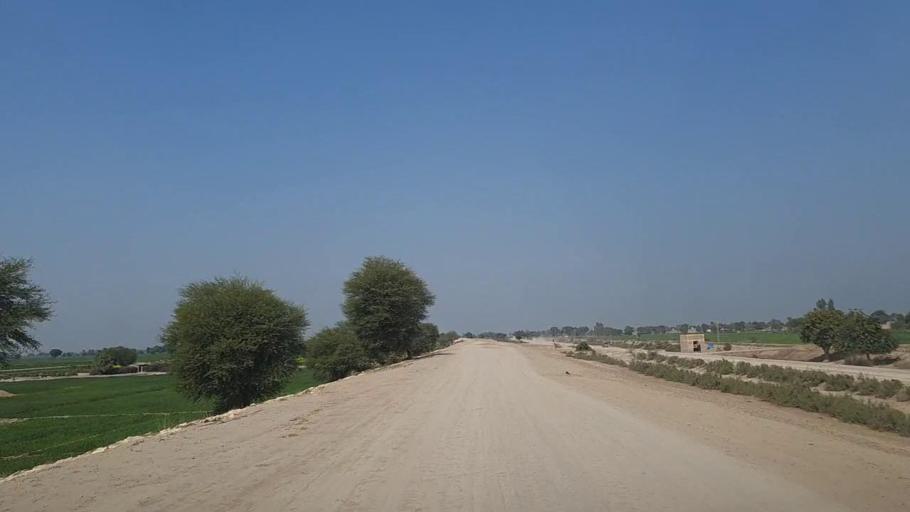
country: PK
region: Sindh
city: Moro
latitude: 26.7228
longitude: 67.9220
